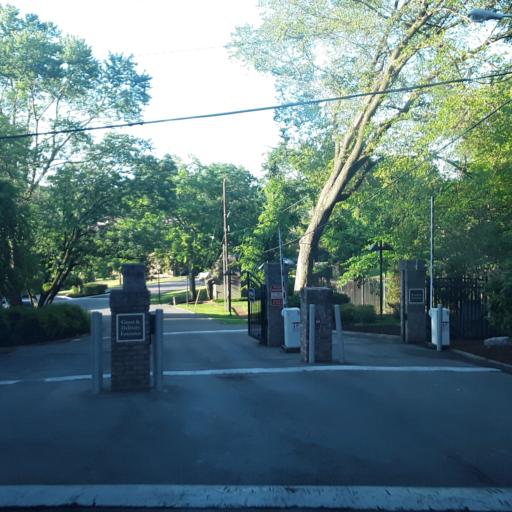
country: US
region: Tennessee
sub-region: Davidson County
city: Oak Hill
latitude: 36.1070
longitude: -86.7254
